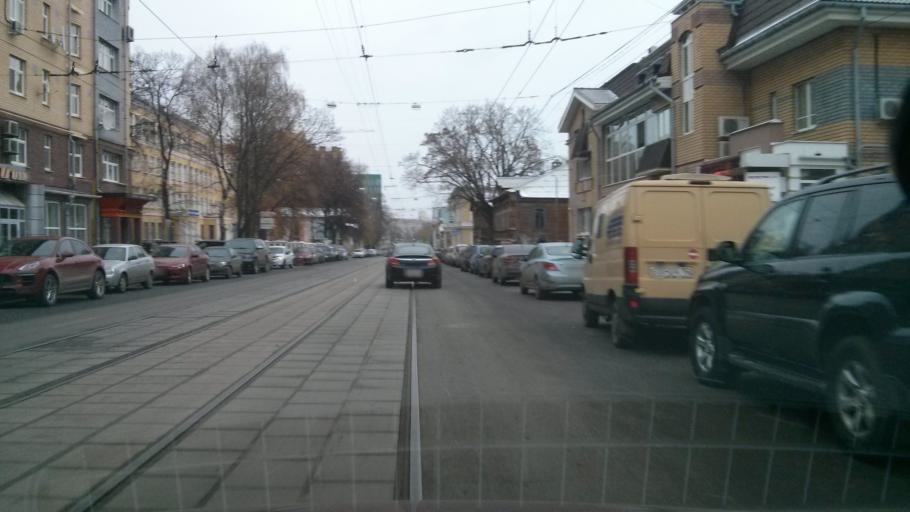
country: RU
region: Nizjnij Novgorod
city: Nizhniy Novgorod
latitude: 56.3243
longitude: 44.0258
